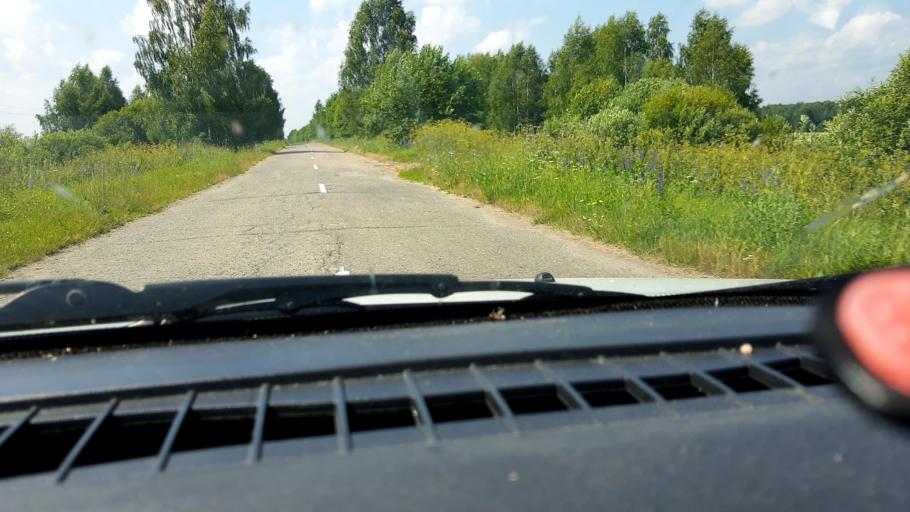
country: RU
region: Nizjnij Novgorod
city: Sharanga
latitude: 57.0552
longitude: 46.5683
